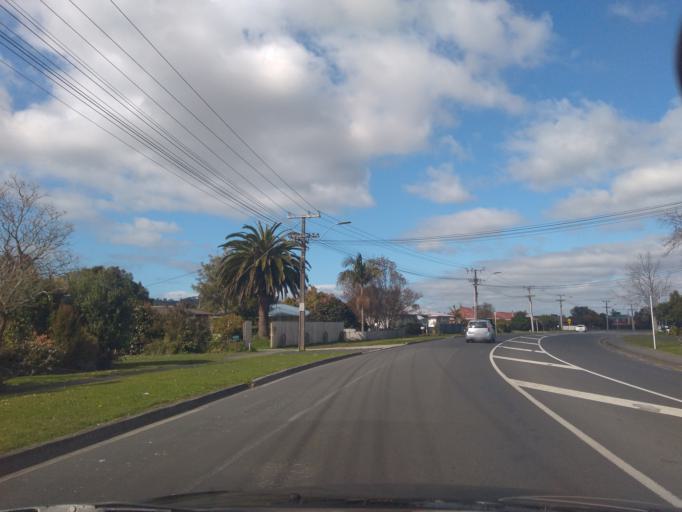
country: NZ
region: Northland
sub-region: Whangarei
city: Whangarei
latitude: -35.6916
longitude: 174.3272
